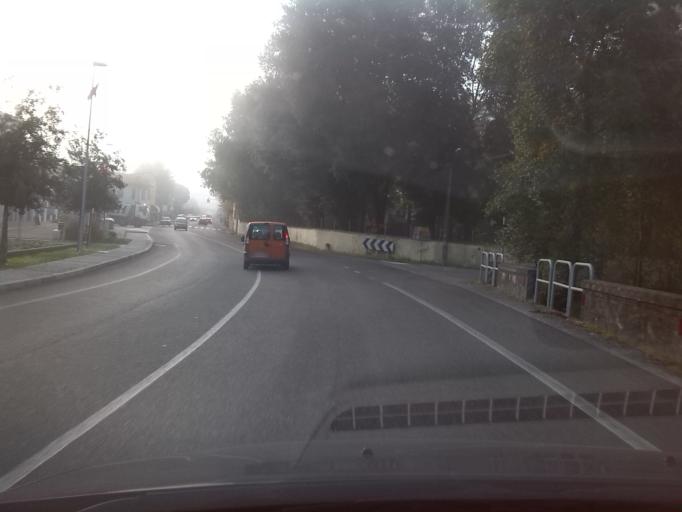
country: IT
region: Friuli Venezia Giulia
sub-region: Provincia di Gorizia
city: Fogliano
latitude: 45.8478
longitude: 13.4874
